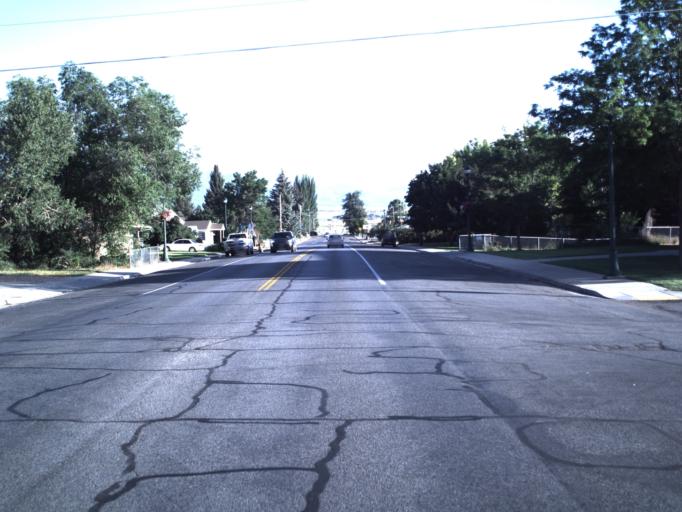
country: US
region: Utah
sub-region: Sanpete County
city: Fairview
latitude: 39.6266
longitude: -111.4393
